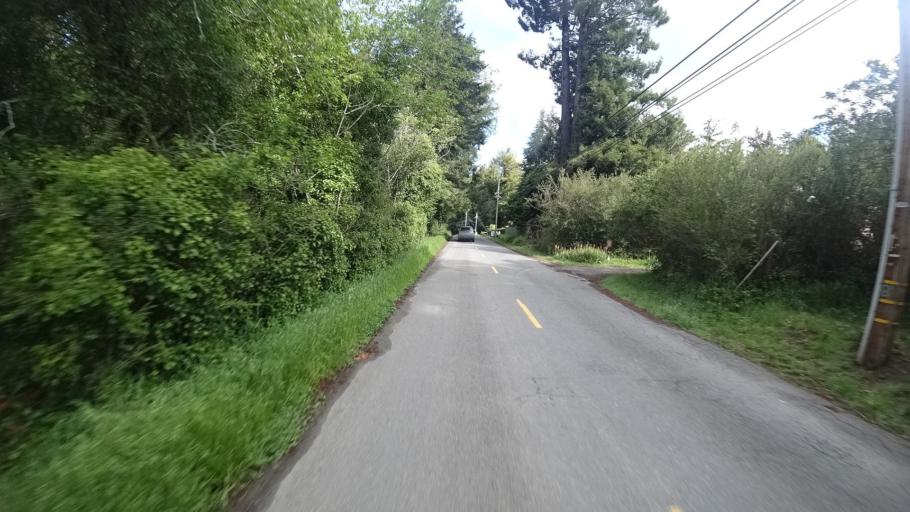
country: US
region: California
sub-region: Humboldt County
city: Westhaven-Moonstone
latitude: 41.0425
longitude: -124.1114
